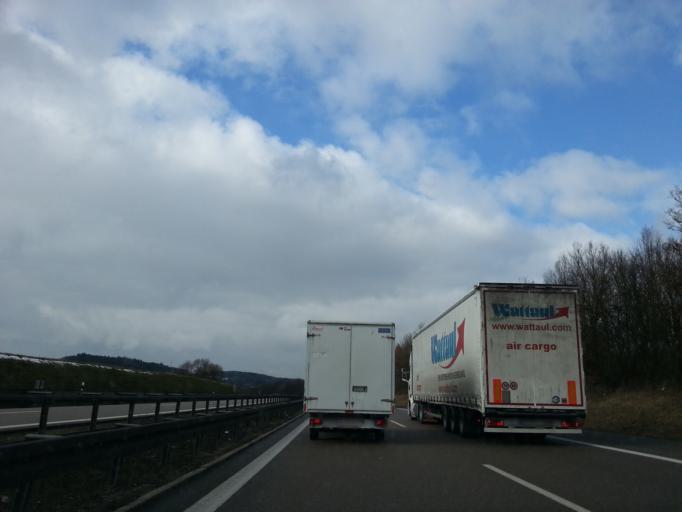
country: DE
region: Bavaria
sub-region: Upper Palatinate
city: Velburg
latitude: 49.2410
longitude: 11.6336
